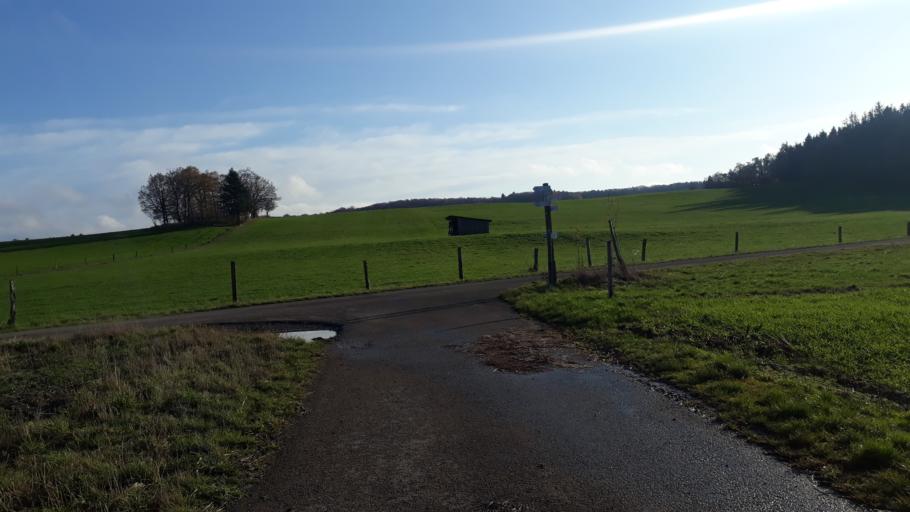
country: DE
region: North Rhine-Westphalia
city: Marsberg
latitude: 51.3742
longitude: 8.7605
